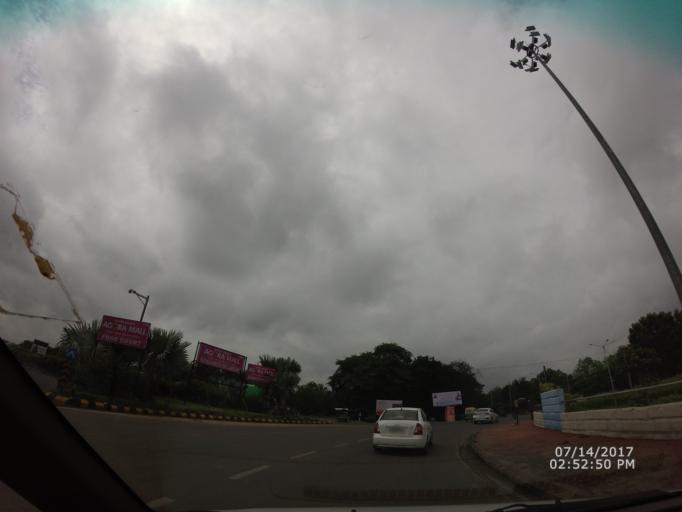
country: IN
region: Gujarat
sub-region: Ahmadabad
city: Naroda
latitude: 23.1168
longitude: 72.6310
